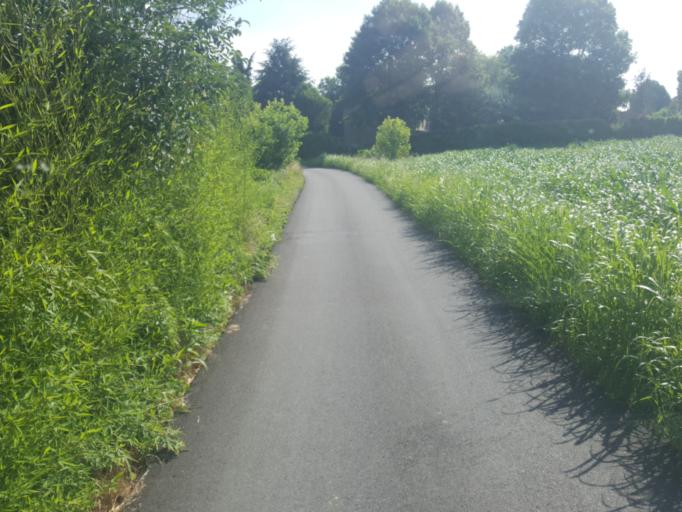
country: IT
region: Lombardy
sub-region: Provincia di Cremona
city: Crema
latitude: 45.3469
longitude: 9.6667
